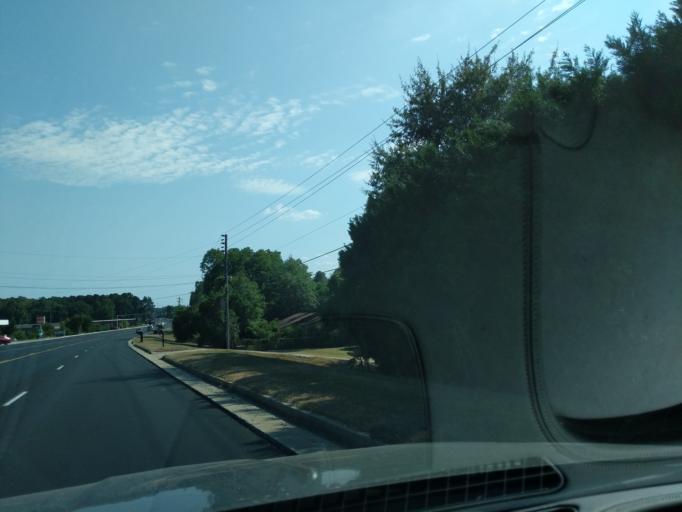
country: US
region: Georgia
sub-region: Columbia County
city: Evans
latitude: 33.4955
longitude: -82.1380
